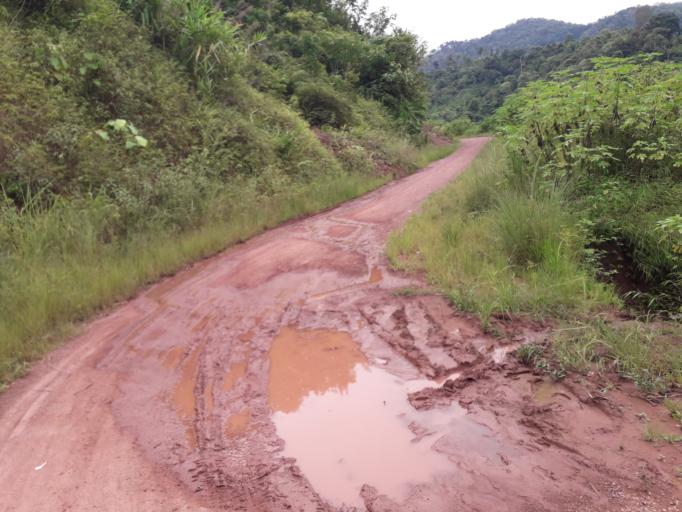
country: CN
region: Yunnan
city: Menglie
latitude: 22.2463
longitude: 101.6098
